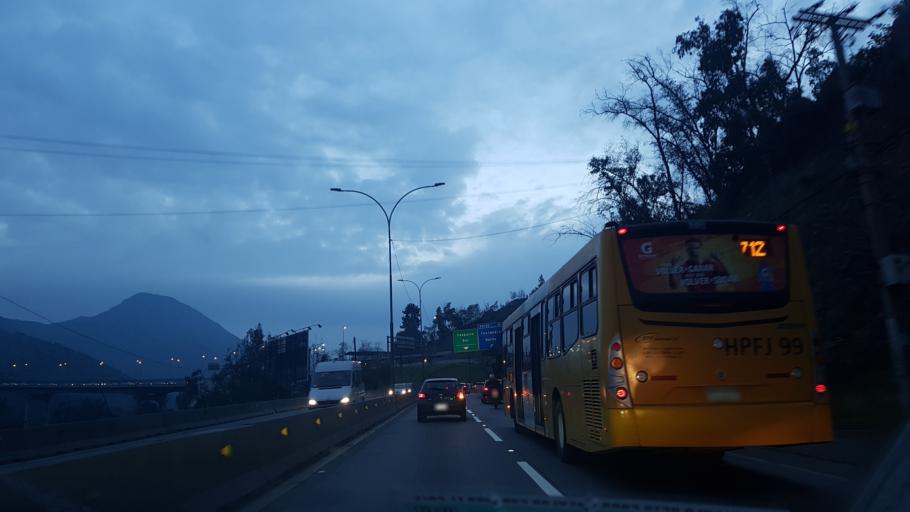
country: CL
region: Santiago Metropolitan
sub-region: Provincia de Santiago
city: Villa Presidente Frei, Nunoa, Santiago, Chile
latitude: -33.3901
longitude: -70.6037
